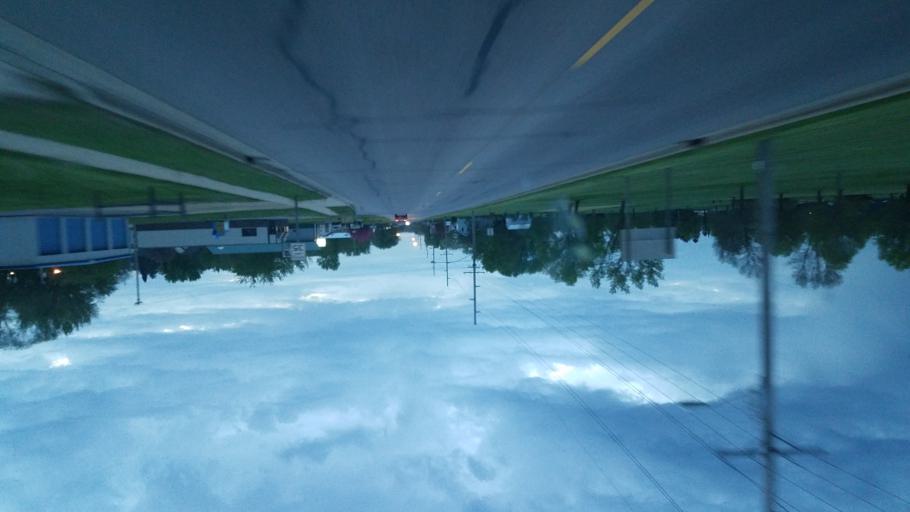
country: US
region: Wisconsin
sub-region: Juneau County
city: Elroy
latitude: 43.6827
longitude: -90.2661
